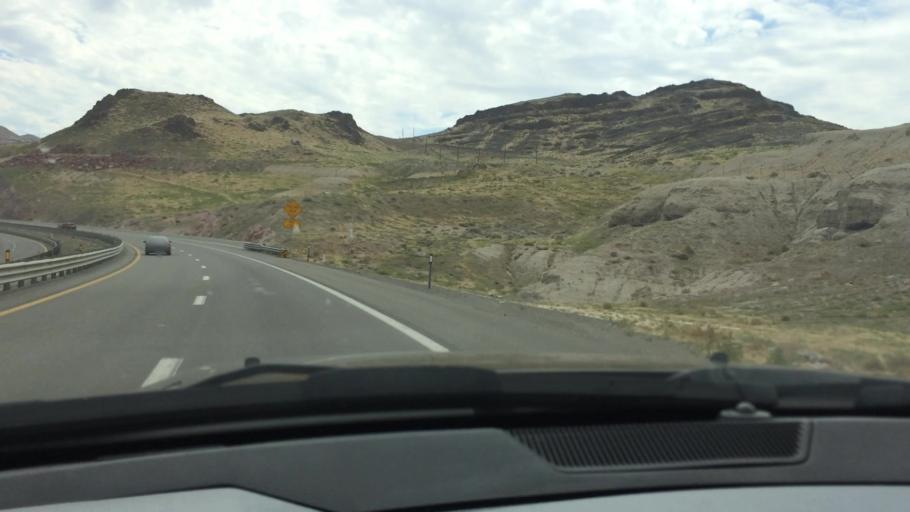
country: US
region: Nevada
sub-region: Lyon County
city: Fernley
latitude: 39.5970
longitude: -119.3629
